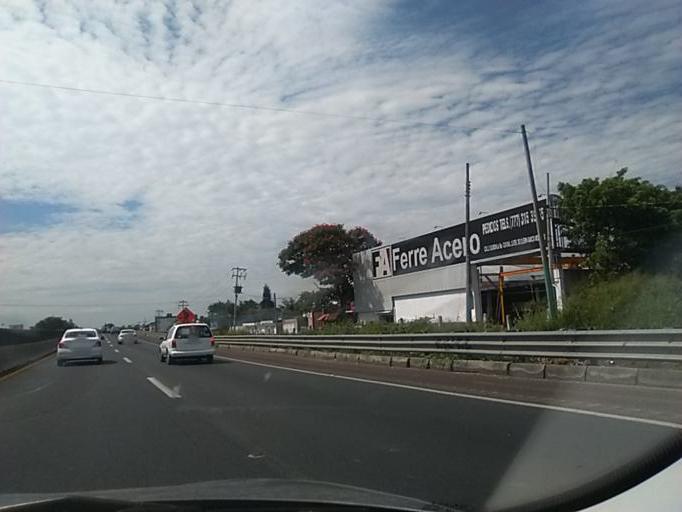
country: MX
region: Morelos
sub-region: Cuernavaca
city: Cuernavaca
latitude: 18.9173
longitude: -99.2048
